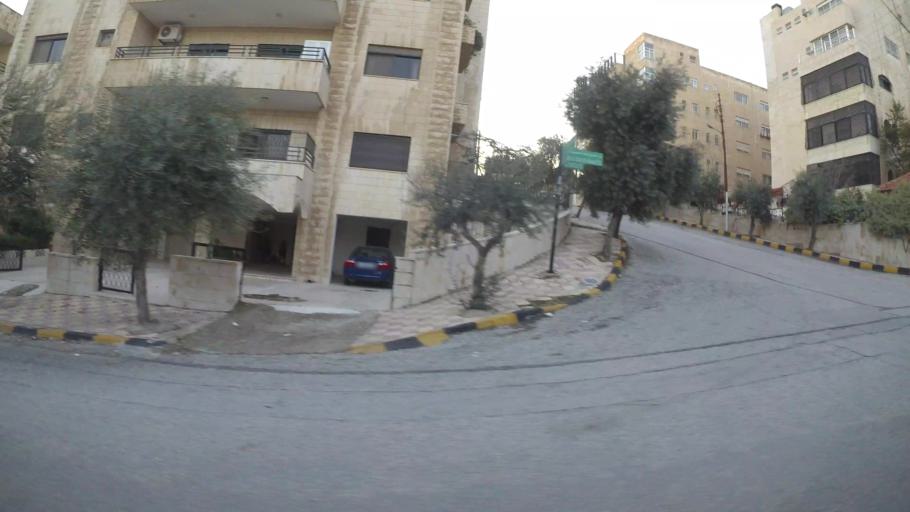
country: JO
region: Amman
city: Al Jubayhah
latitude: 31.9963
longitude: 35.8633
